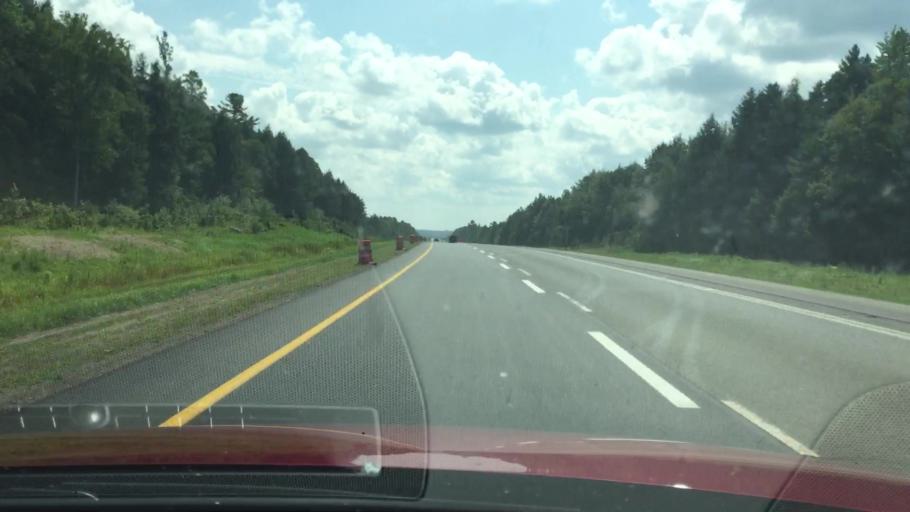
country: US
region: Maine
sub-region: Penobscot County
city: Medway
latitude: 45.6700
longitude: -68.4995
